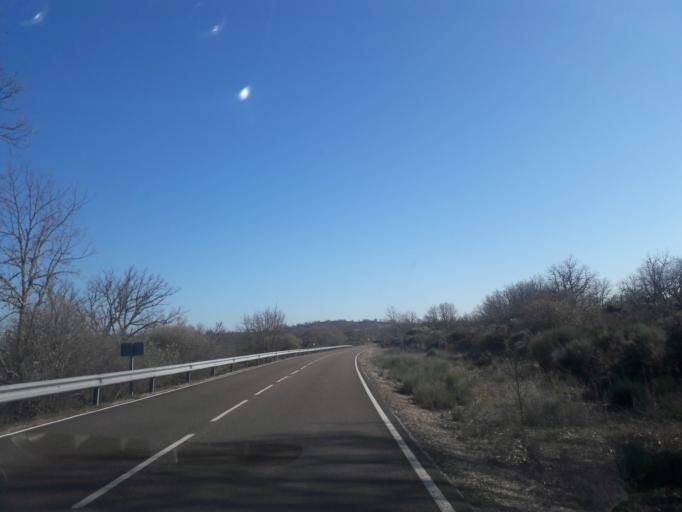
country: ES
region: Castille and Leon
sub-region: Provincia de Salamanca
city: Cabeza del Caballo
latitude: 41.0920
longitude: -6.5570
